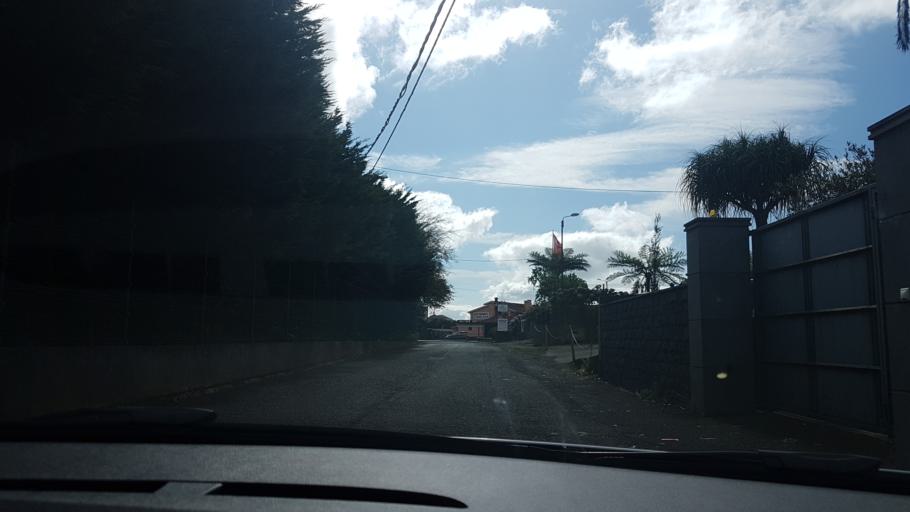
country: PT
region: Madeira
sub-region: Santa Cruz
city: Santa Cruz
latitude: 32.7275
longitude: -16.8211
